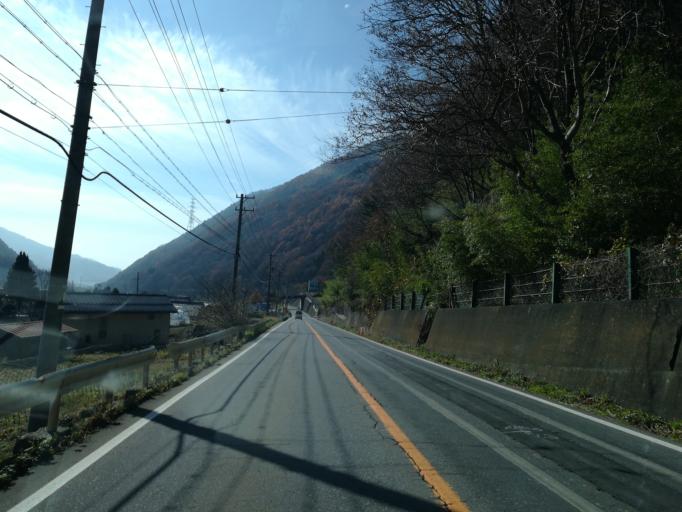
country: JP
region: Nagano
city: Ueda
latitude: 36.4798
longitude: 138.3485
